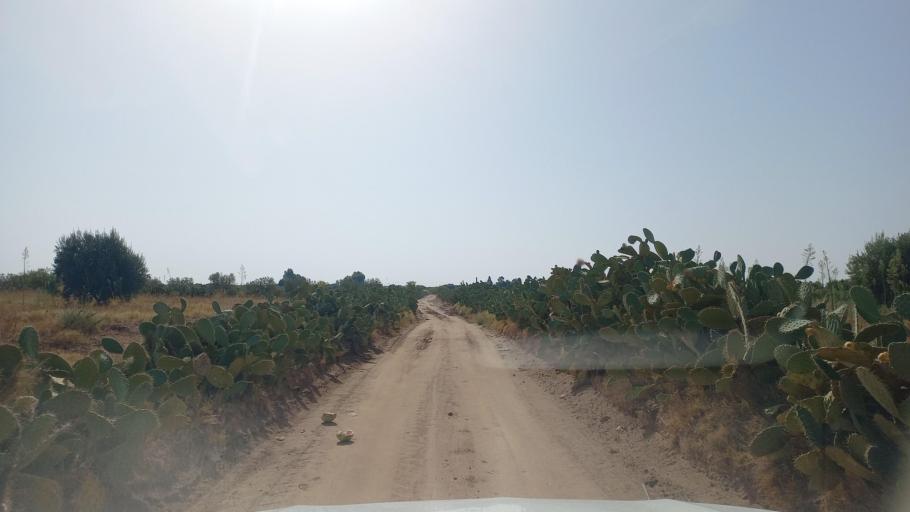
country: TN
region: Al Qasrayn
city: Kasserine
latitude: 35.2476
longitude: 9.0363
